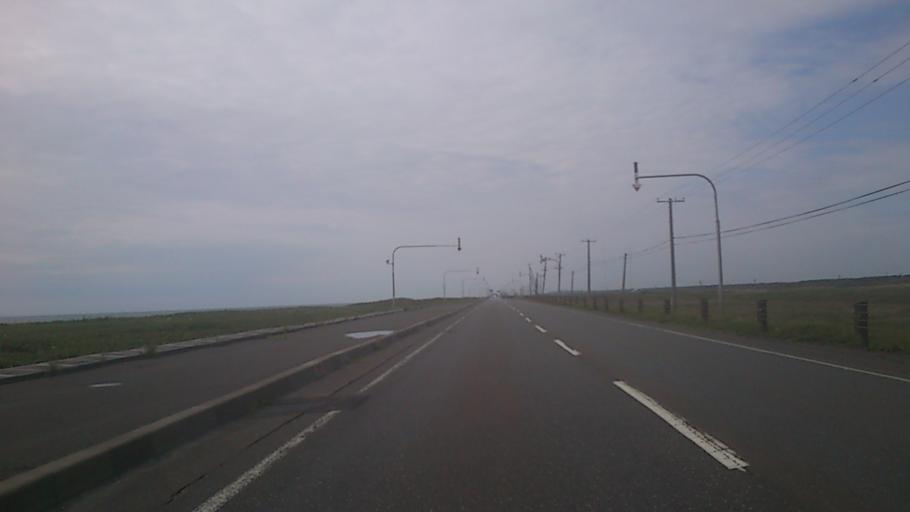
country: JP
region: Hokkaido
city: Makubetsu
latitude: 44.9856
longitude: 141.6906
